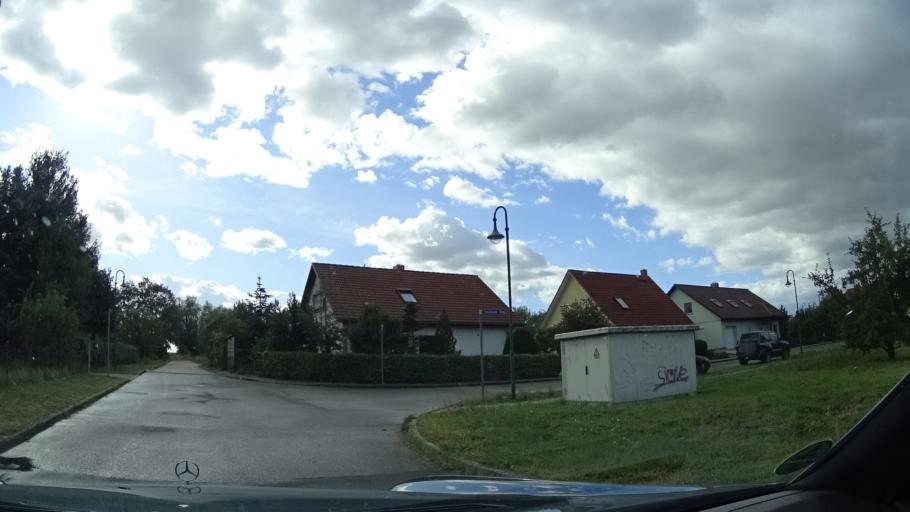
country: DE
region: Brandenburg
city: Neuruppin
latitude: 52.8896
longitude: 12.7921
